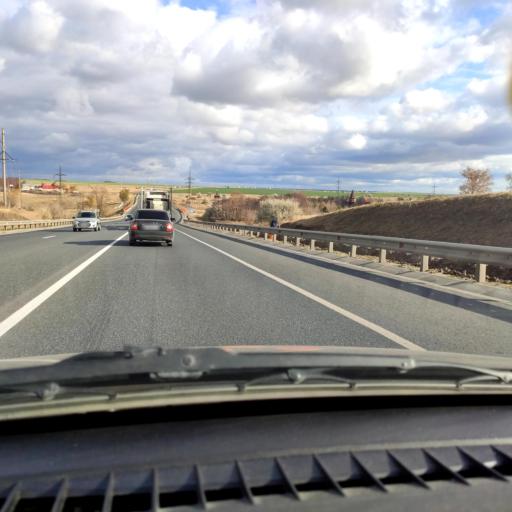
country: RU
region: Samara
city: Varlamovo
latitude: 53.2015
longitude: 48.3785
